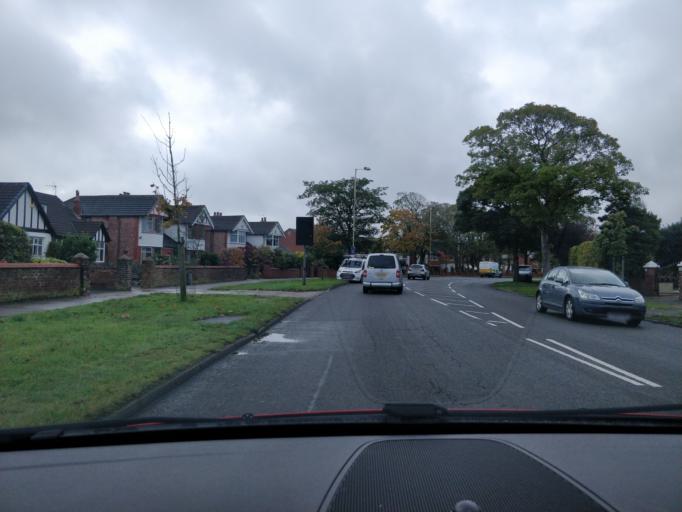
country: GB
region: England
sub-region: Sefton
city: Southport
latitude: 53.6100
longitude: -3.0228
